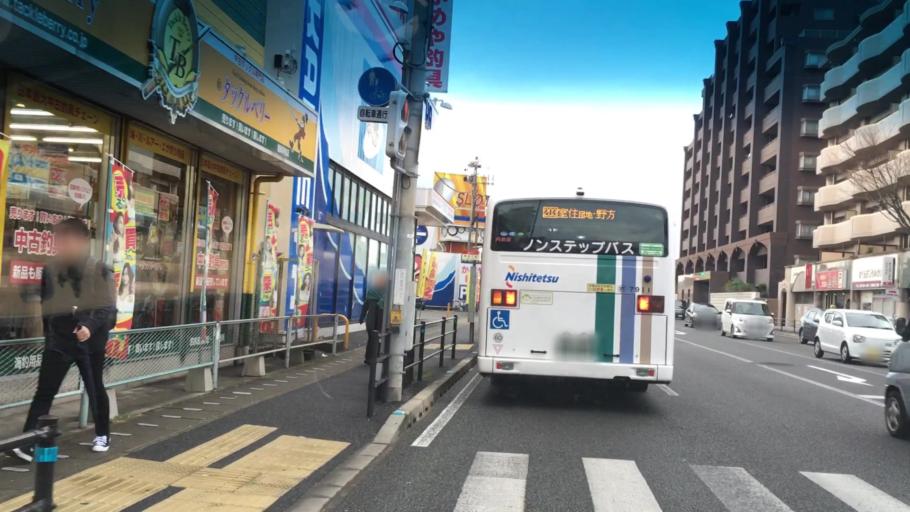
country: JP
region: Fukuoka
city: Fukuoka-shi
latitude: 33.5674
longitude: 130.3401
